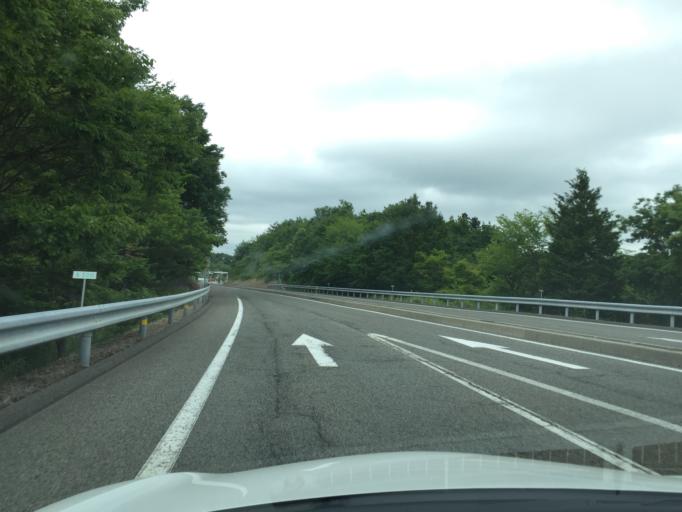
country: JP
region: Fukushima
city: Miharu
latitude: 37.4400
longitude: 140.5228
